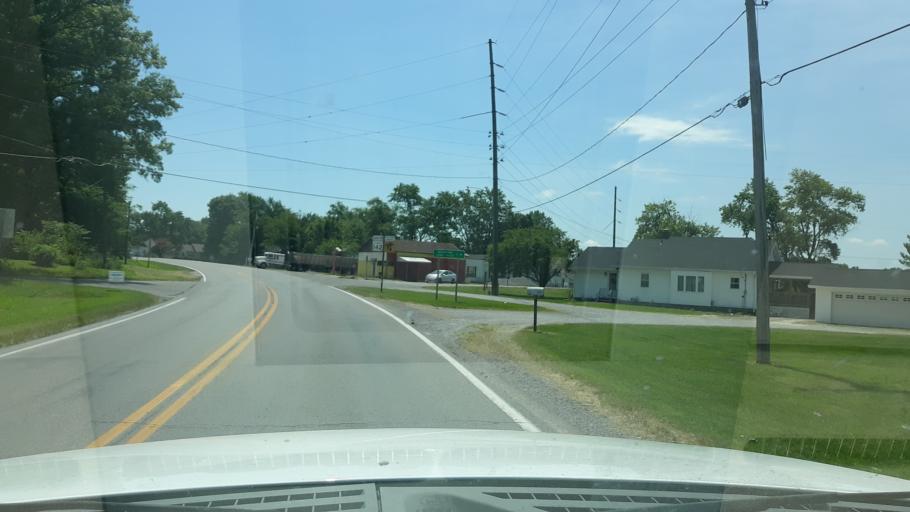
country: US
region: Illinois
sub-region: Saline County
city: Eldorado
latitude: 37.8056
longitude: -88.4389
